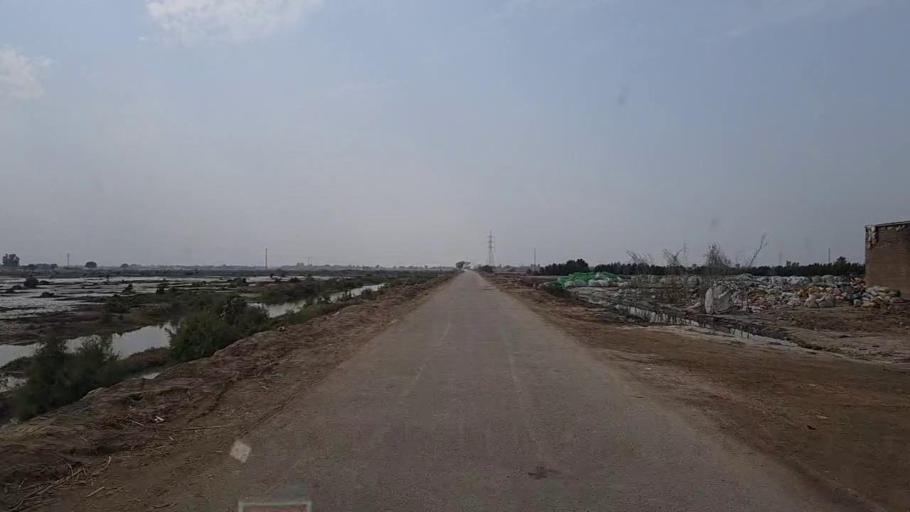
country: PK
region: Sindh
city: Mirwah Gorchani
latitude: 25.3371
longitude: 69.0488
